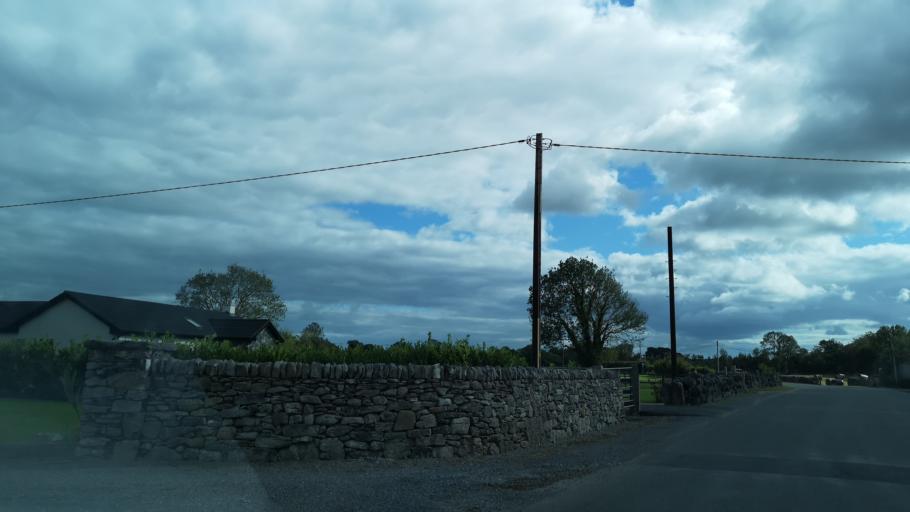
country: IE
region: Connaught
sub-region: County Galway
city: Moycullen
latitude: 53.3578
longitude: -9.1746
